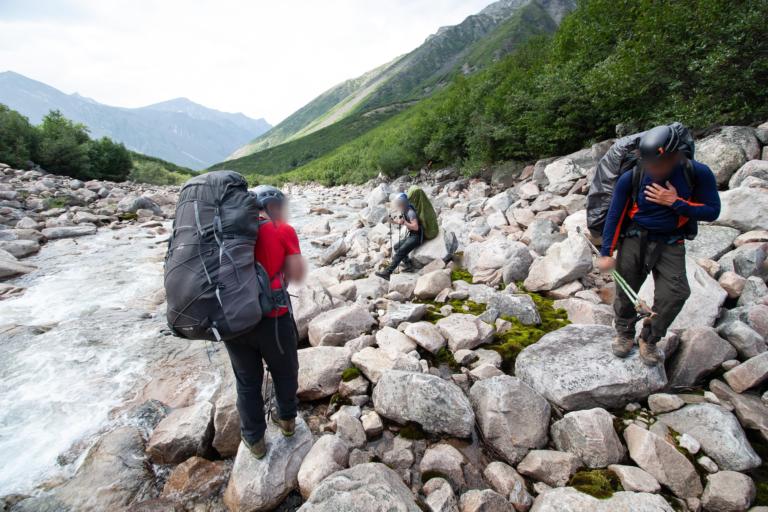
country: RU
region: Respublika Buryatiya
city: Novyy Uoyan
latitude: 56.3196
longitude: 111.2062
